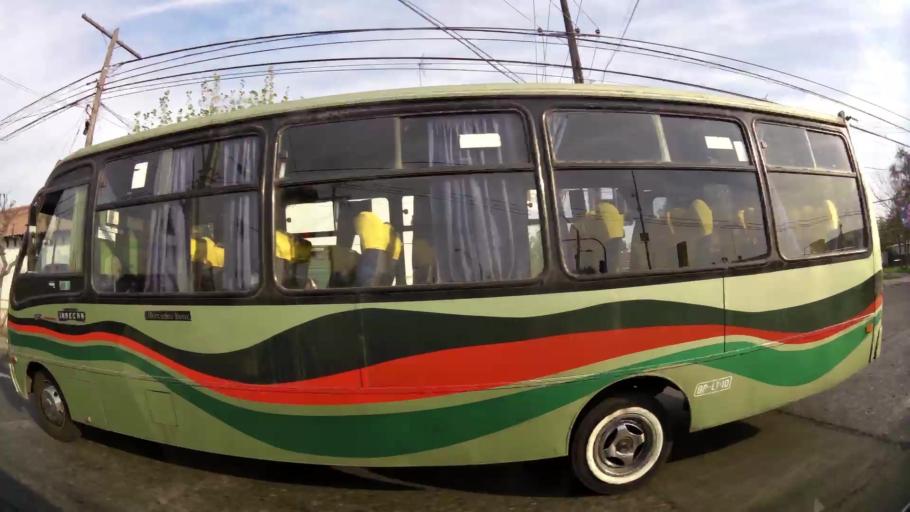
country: CL
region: Santiago Metropolitan
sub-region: Provincia de Talagante
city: Penaflor
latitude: -33.5695
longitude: -70.8158
